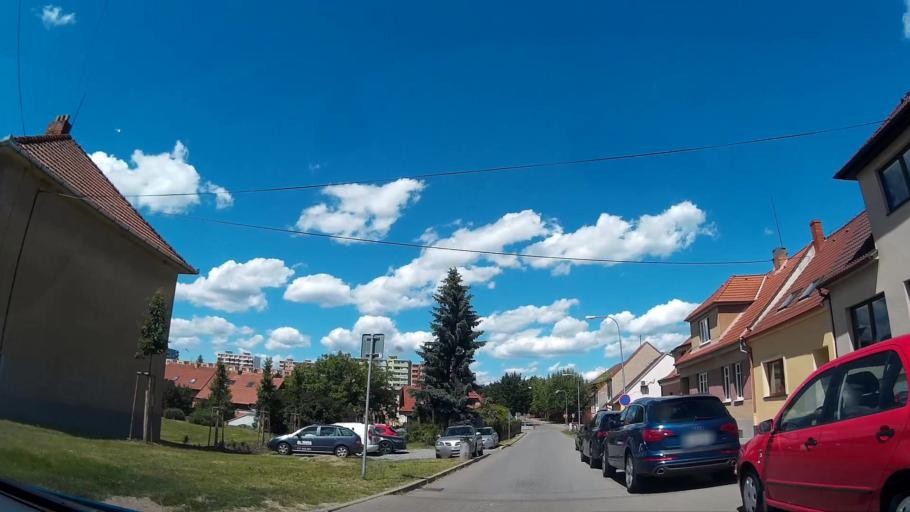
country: CZ
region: South Moravian
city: Ivancice
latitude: 49.1030
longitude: 16.3685
